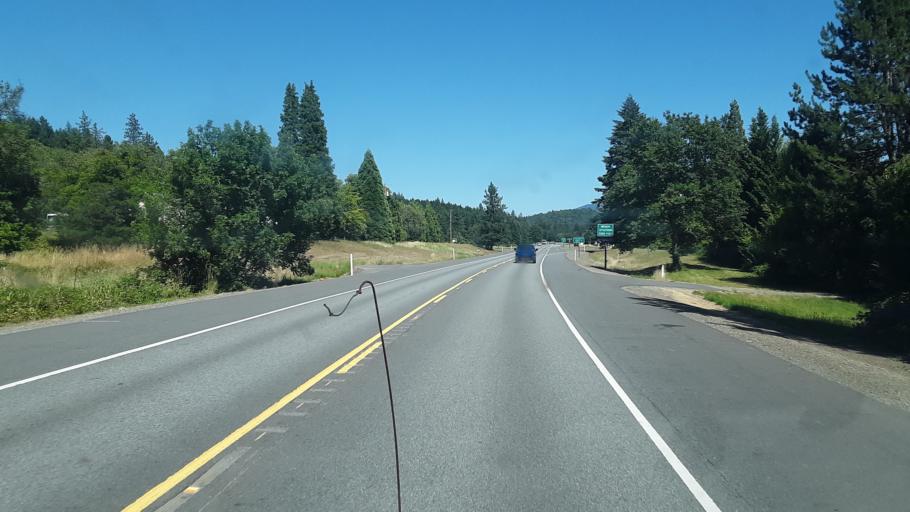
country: US
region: Oregon
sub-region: Josephine County
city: Redwood
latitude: 42.3831
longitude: -123.4826
